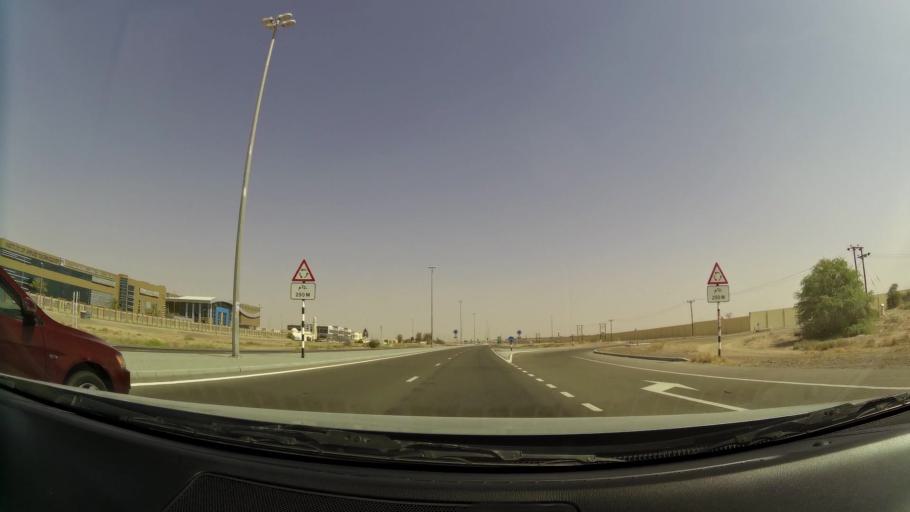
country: OM
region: Al Buraimi
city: Al Buraymi
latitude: 24.3043
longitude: 55.7629
